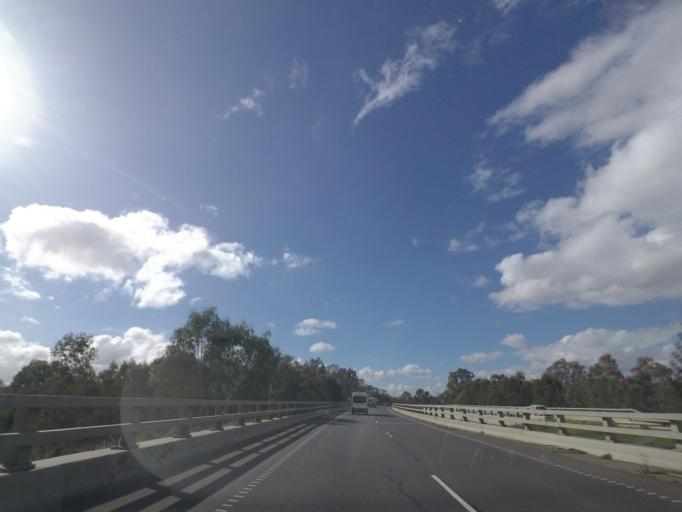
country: AU
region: New South Wales
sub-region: Albury Municipality
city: South Albury
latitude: -36.1026
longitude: 146.9068
